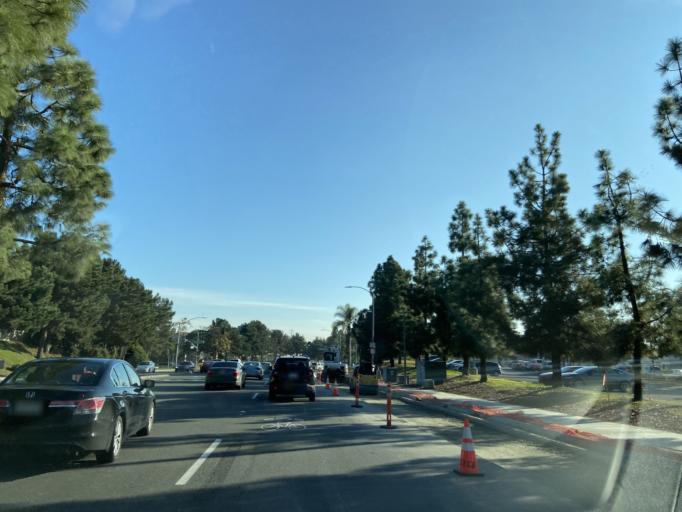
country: US
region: California
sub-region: San Diego County
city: Bonita
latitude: 32.6417
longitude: -116.9665
